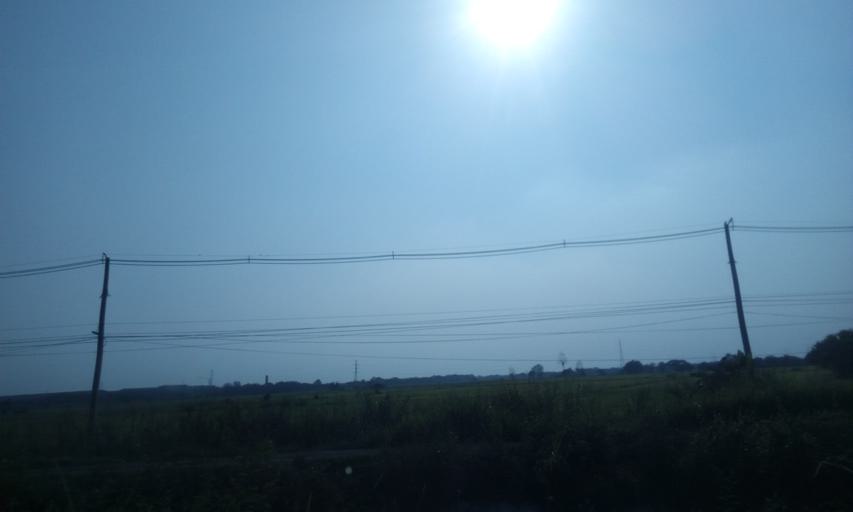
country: TH
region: Sing Buri
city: Phrom Buri
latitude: 14.8156
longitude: 100.4338
